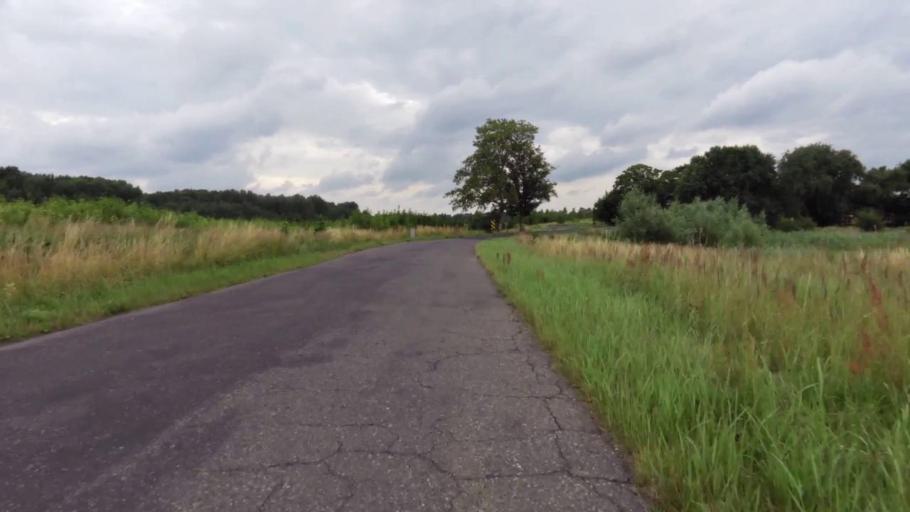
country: PL
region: West Pomeranian Voivodeship
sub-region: Powiat mysliborski
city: Mysliborz
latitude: 52.9613
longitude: 14.8843
